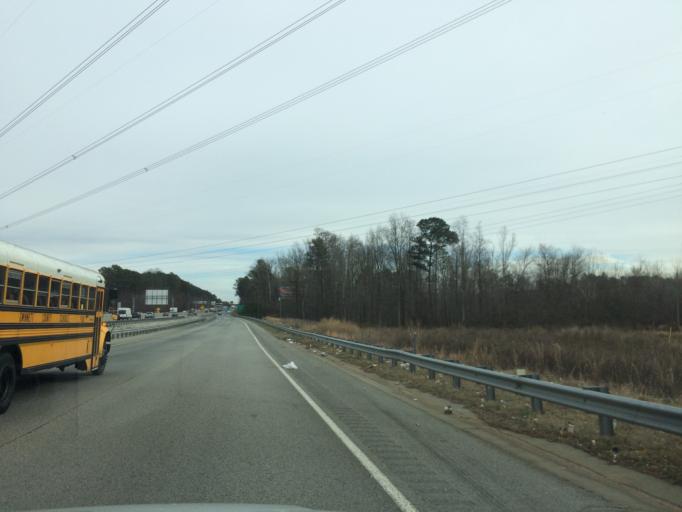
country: US
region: Georgia
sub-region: Gwinnett County
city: Duluth
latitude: 33.9632
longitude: -84.0893
